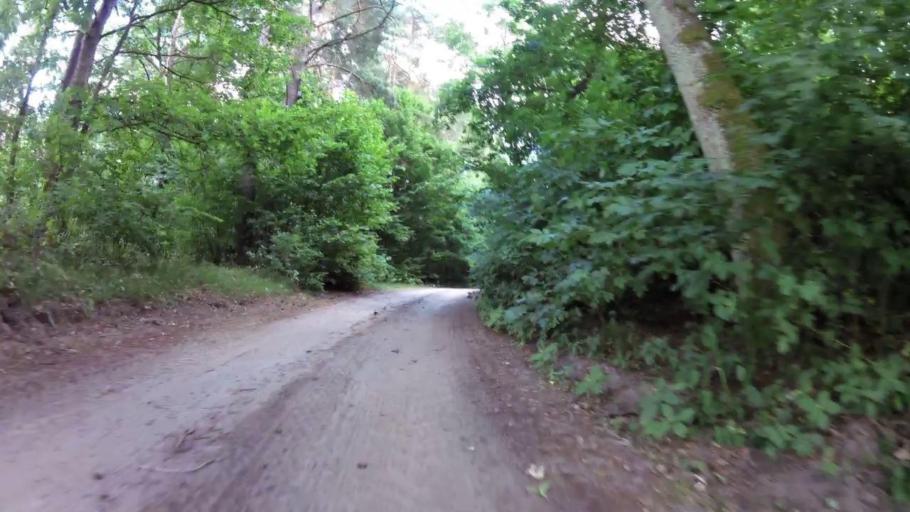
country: PL
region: West Pomeranian Voivodeship
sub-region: Powiat swidwinski
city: Swidwin
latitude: 53.6805
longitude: 15.7368
